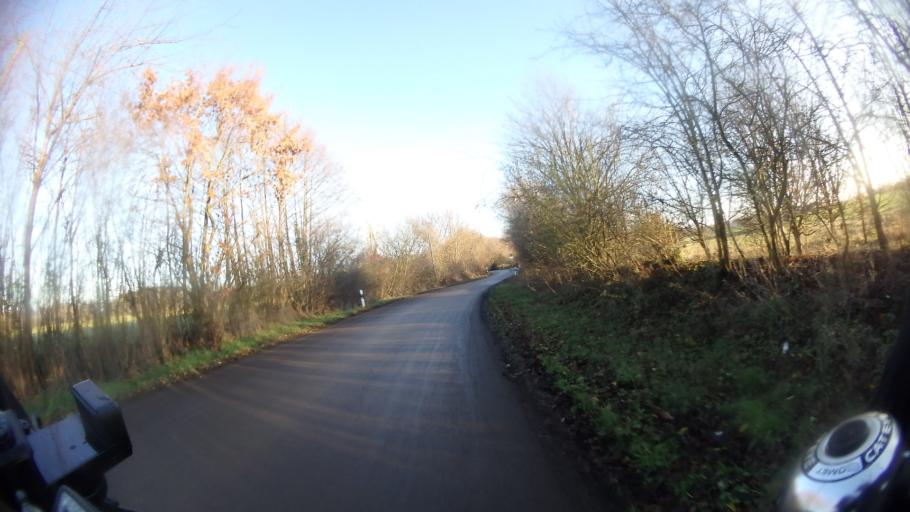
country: DE
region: Schleswig-Holstein
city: Travemuende
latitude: 53.9842
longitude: 10.8678
